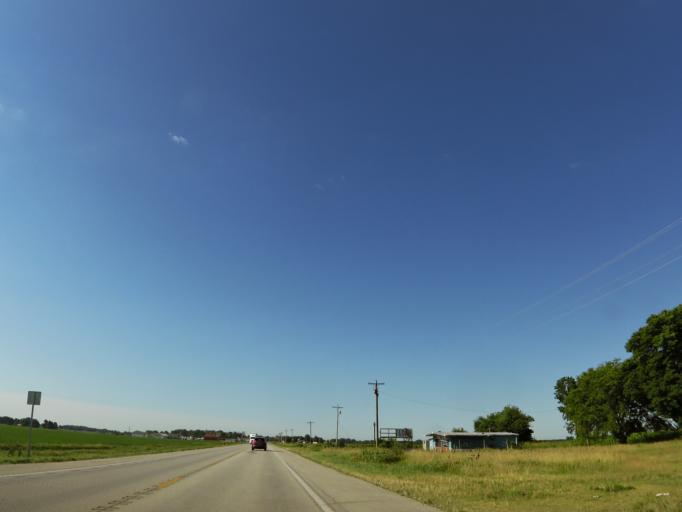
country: US
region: Arkansas
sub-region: Clay County
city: Corning
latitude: 36.5076
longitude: -90.5397
